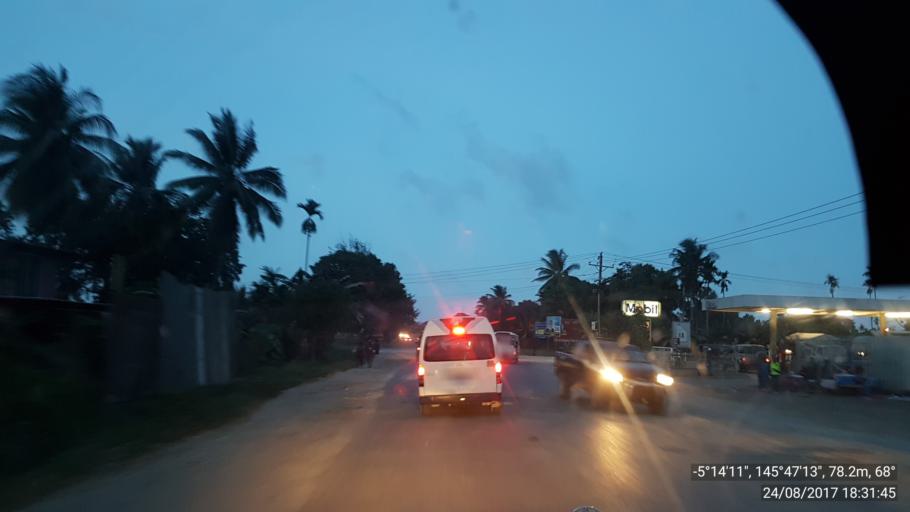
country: PG
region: Madang
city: Madang
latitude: -5.2367
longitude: 145.7872
